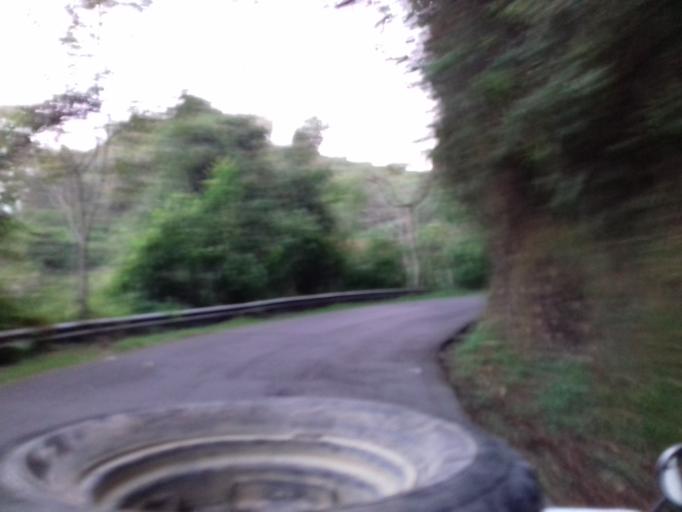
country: CO
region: Quindio
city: Salento
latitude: 4.6418
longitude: -75.5736
